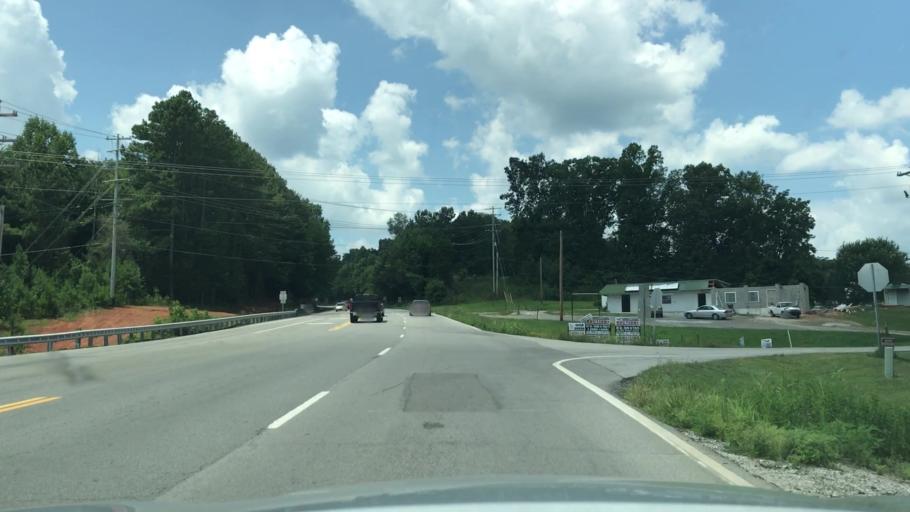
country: US
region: Tennessee
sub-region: Overton County
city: Livingston
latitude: 36.4393
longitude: -85.2677
